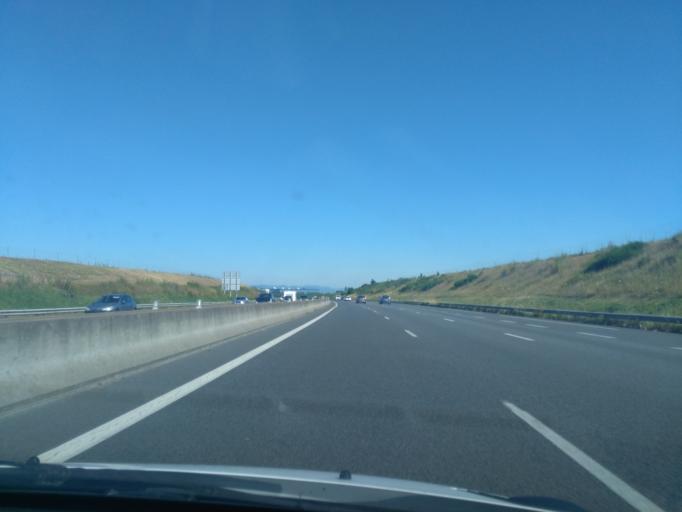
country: FR
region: Rhone-Alpes
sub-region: Departement de l'Ain
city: Civrieux
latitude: 45.8955
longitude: 4.8886
